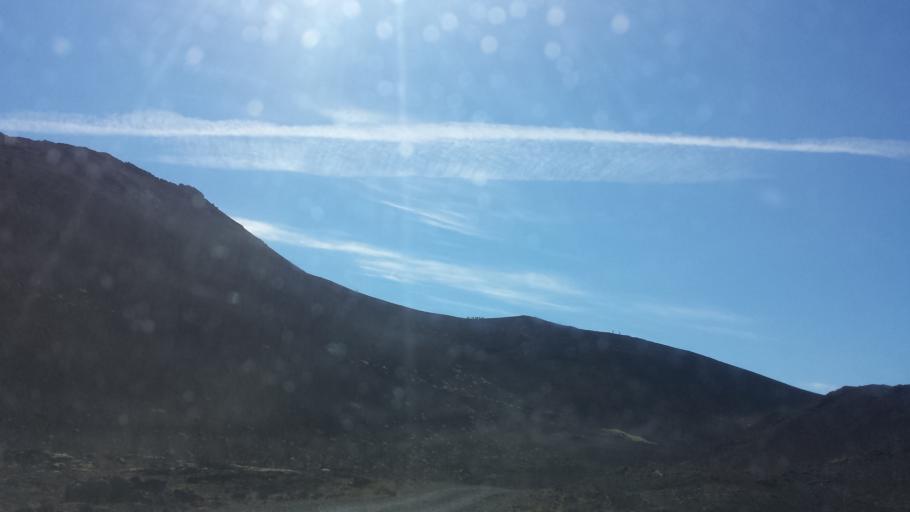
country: IS
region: South
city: Vestmannaeyjar
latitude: 63.4362
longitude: -20.2471
